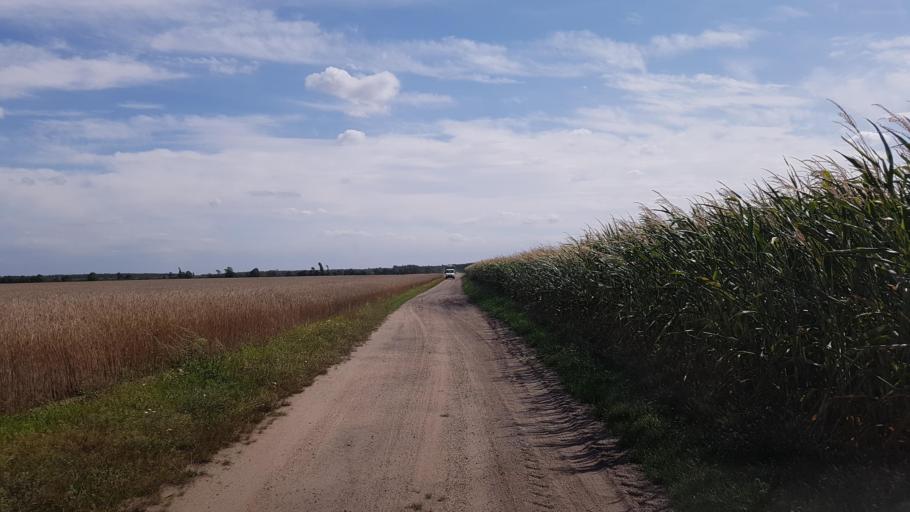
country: DE
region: Brandenburg
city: Muhlberg
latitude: 51.4624
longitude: 13.2821
